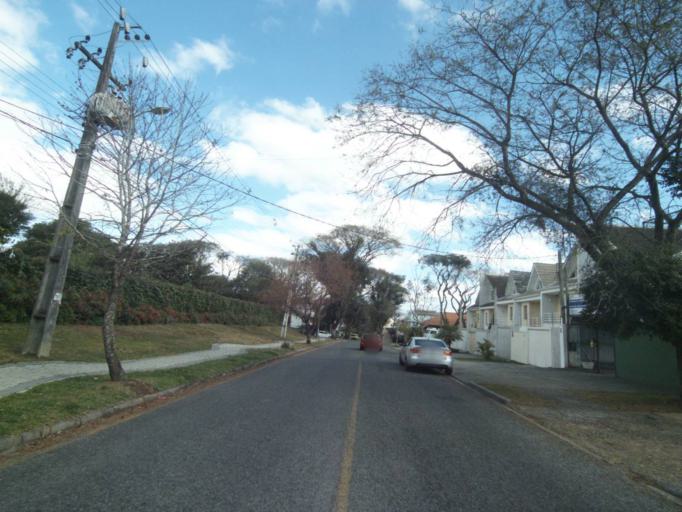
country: BR
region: Parana
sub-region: Curitiba
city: Curitiba
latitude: -25.4547
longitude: -49.2757
